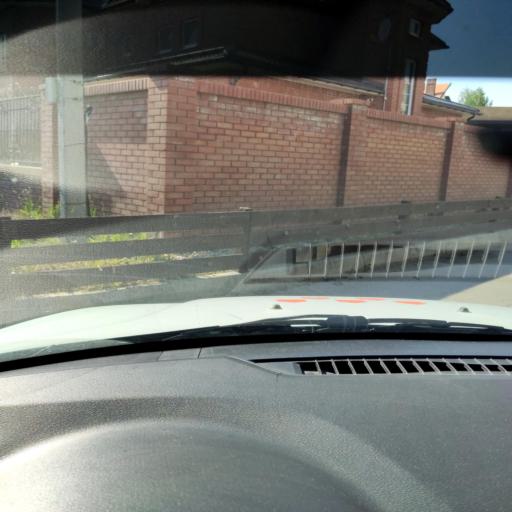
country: RU
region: Samara
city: Podstepki
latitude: 53.5102
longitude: 49.1421
